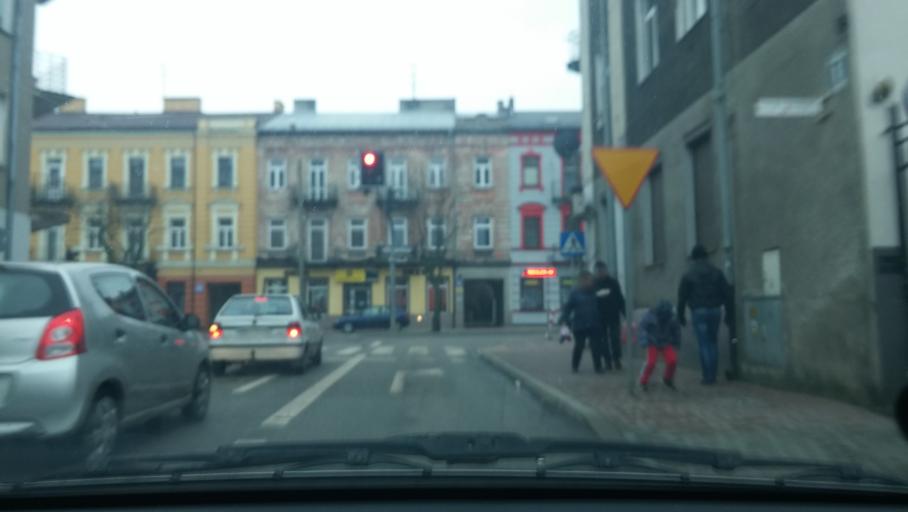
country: PL
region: Masovian Voivodeship
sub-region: Siedlce
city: Siedlce
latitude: 52.1680
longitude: 22.2659
